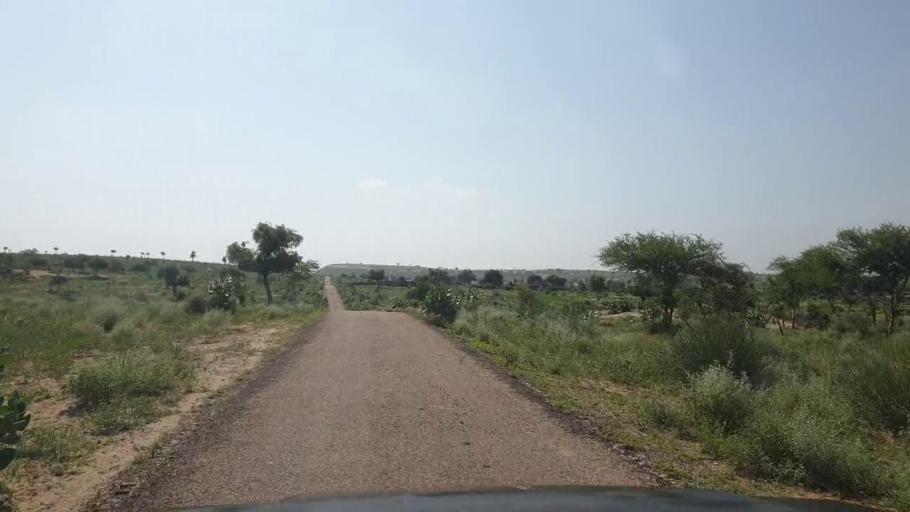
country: PK
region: Sindh
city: Islamkot
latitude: 25.1706
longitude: 70.3994
